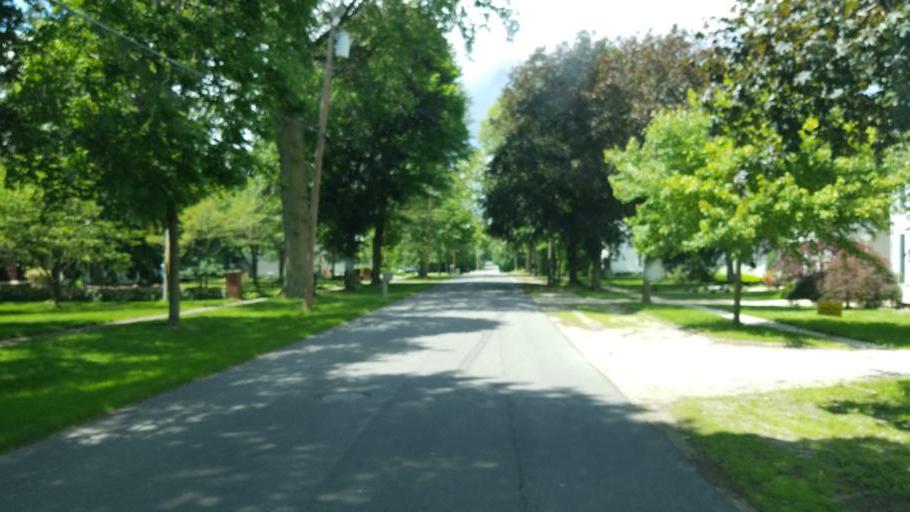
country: US
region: Ohio
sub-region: Erie County
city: Milan
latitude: 41.2958
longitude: -82.6008
